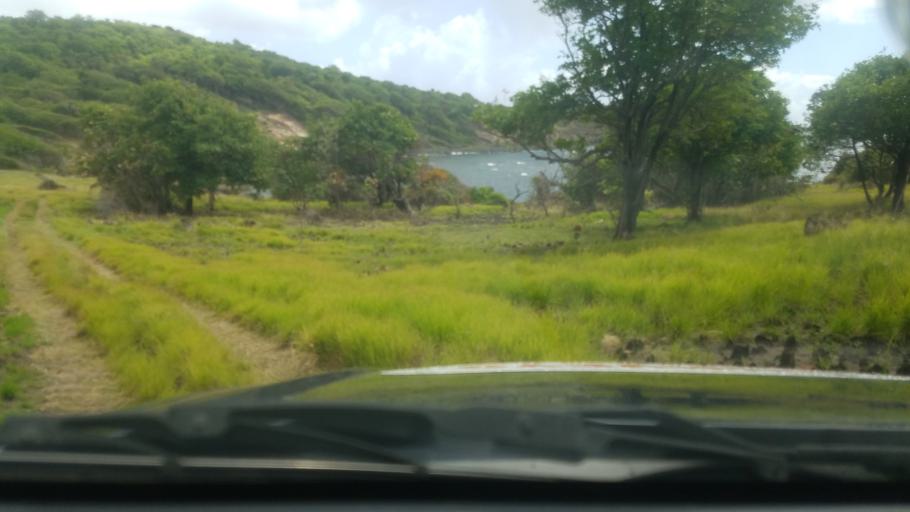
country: LC
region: Praslin
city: Praslin
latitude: 13.8683
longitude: -60.8865
